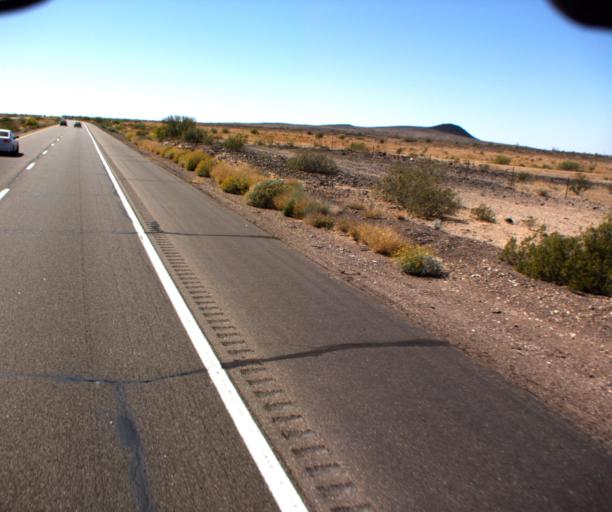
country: US
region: Arizona
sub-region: Maricopa County
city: Gila Bend
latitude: 32.8779
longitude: -113.1148
